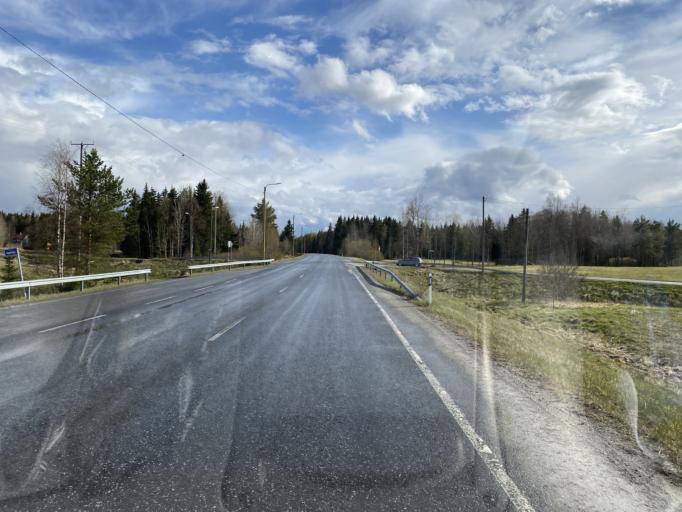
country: FI
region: Pirkanmaa
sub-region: Etelae-Pirkanmaa
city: Viiala
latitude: 61.2203
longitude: 23.7374
